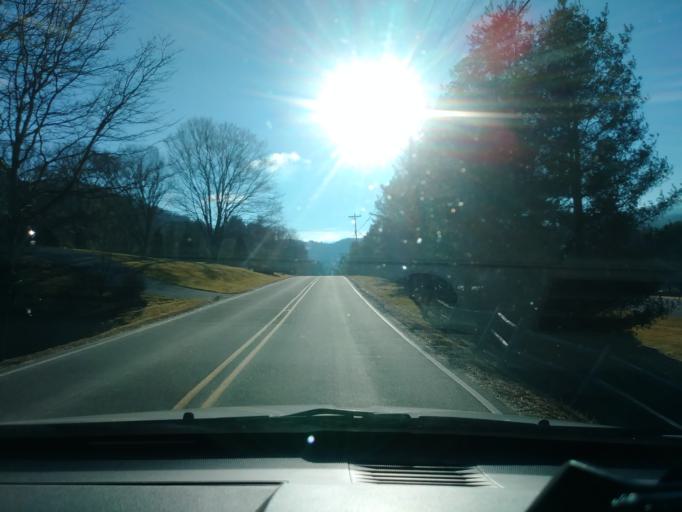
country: US
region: North Carolina
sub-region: Avery County
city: Banner Elk
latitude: 36.1630
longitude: -81.8994
